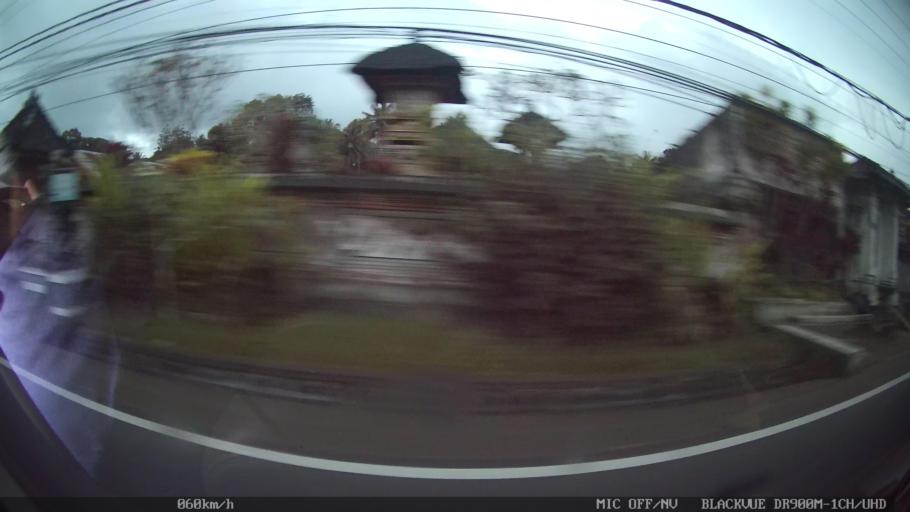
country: ID
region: Bali
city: Badung
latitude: -8.4401
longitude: 115.2442
